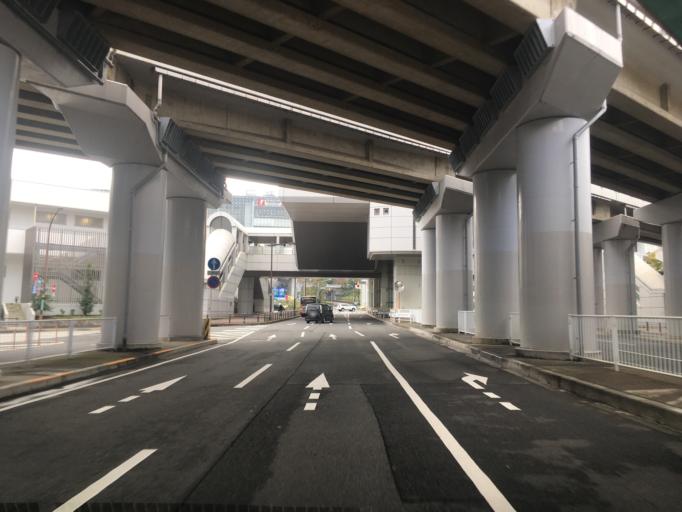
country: JP
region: Tokyo
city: Hino
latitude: 35.6246
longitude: 139.4232
